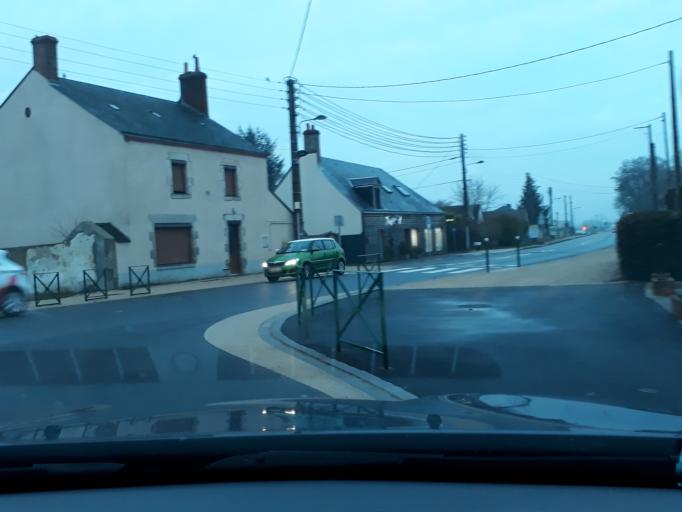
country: FR
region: Centre
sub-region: Departement du Loiret
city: Loury
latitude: 47.9962
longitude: 2.0827
